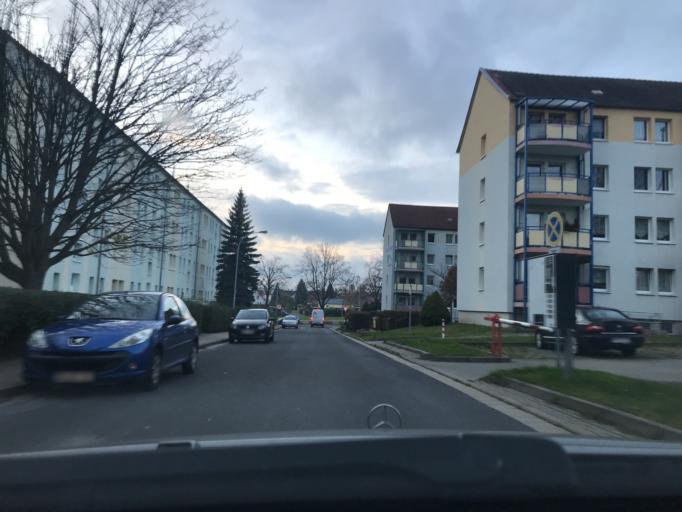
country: DE
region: Thuringia
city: Muehlhausen
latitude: 51.2208
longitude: 10.4731
